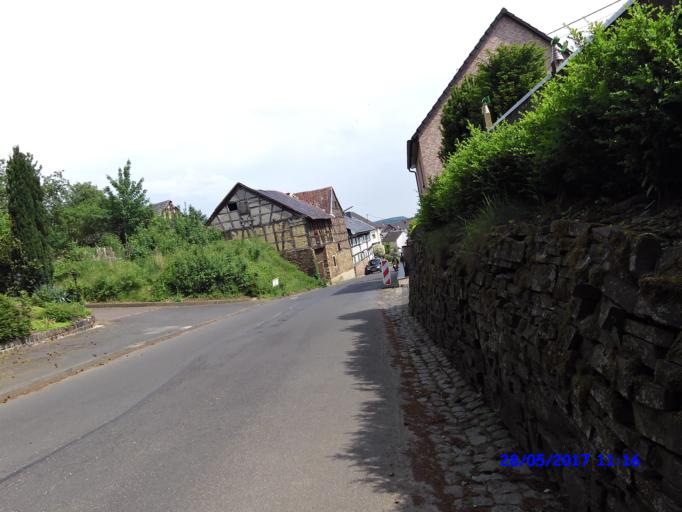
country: DE
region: Rheinland-Pfalz
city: Berg
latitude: 50.5483
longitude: 6.9307
